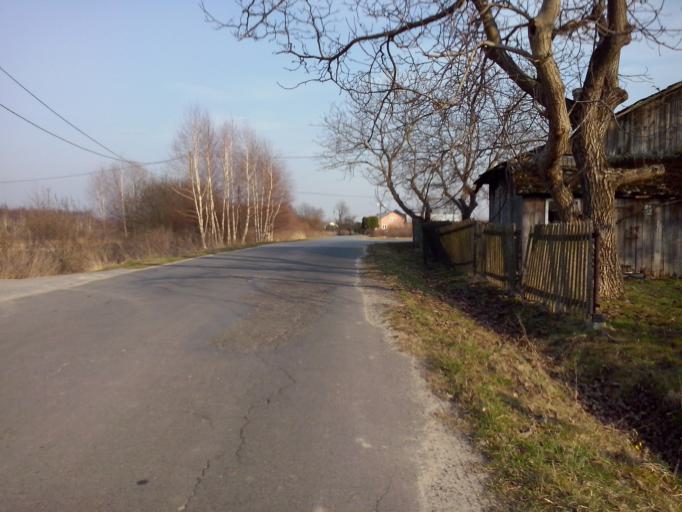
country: PL
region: Subcarpathian Voivodeship
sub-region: Powiat nizanski
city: Krzeszow
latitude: 50.4114
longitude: 22.3554
